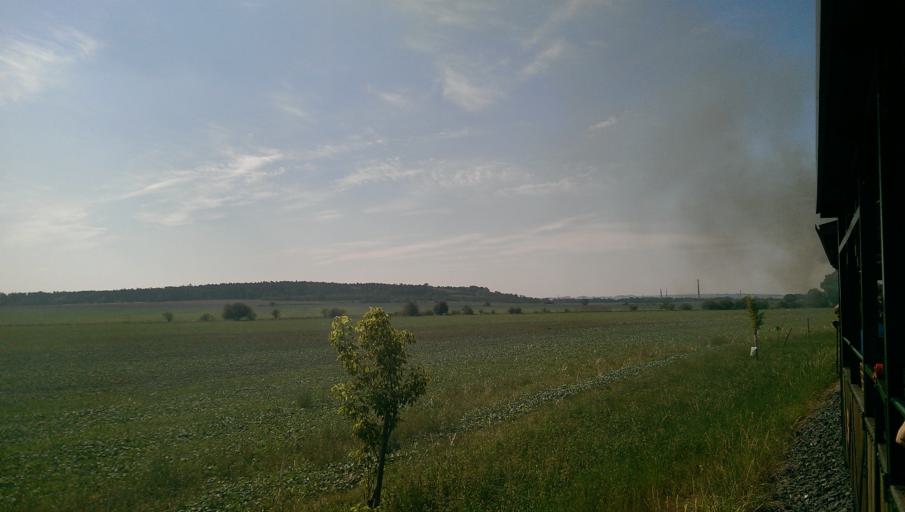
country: CZ
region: Central Bohemia
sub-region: Okres Kolin
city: Kolin
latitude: 50.0530
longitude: 15.2471
